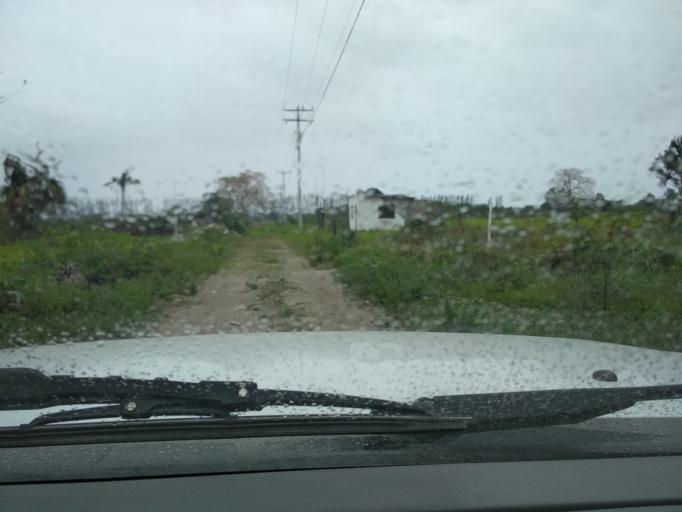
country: MX
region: Veracruz
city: Paso del Toro
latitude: 19.0444
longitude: -96.1314
